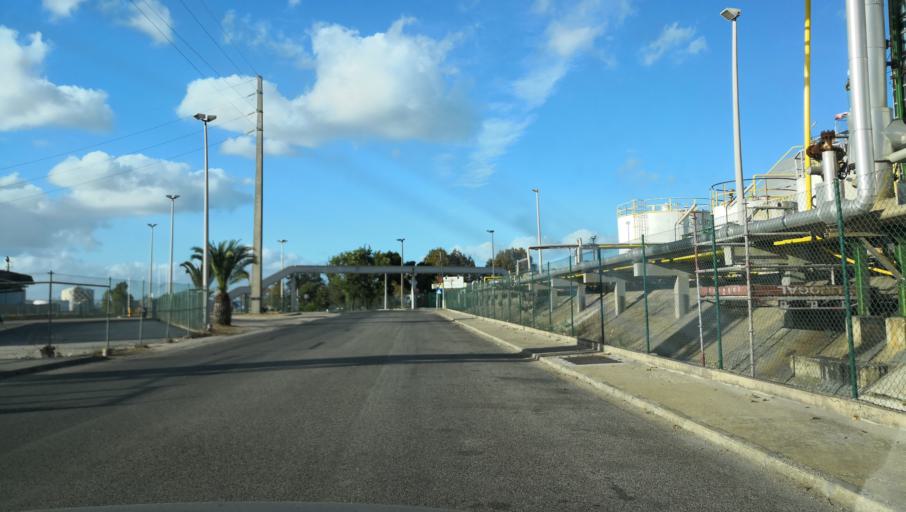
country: PT
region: Setubal
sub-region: Barreiro
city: Barreiro
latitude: 38.6732
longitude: -9.0523
